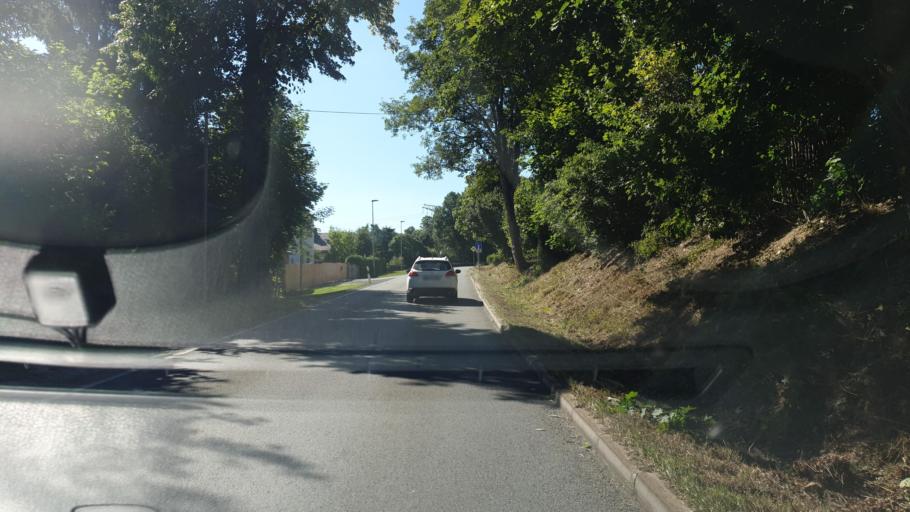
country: DE
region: Saxony
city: Rodewisch
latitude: 50.5214
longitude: 12.4074
